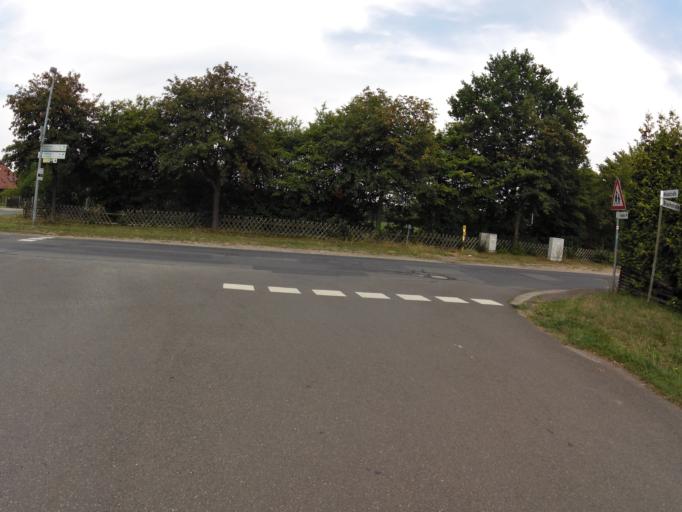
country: DE
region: Lower Saxony
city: Estorf
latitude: 52.5969
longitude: 9.1576
